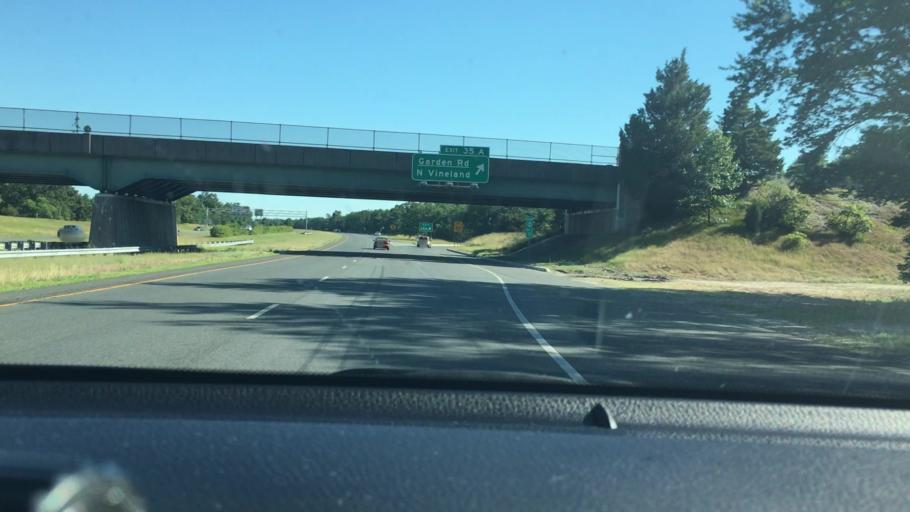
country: US
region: New Jersey
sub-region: Gloucester County
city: Newfield
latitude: 39.5225
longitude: -75.0690
